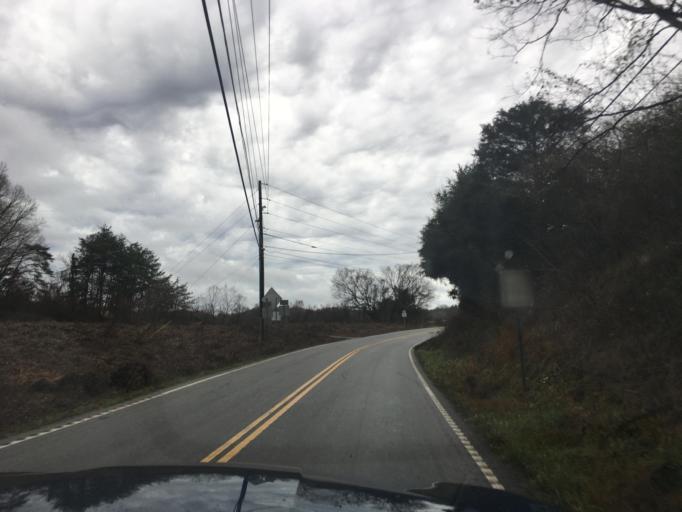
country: US
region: Tennessee
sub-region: Monroe County
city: Madisonville
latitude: 35.3728
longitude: -84.3063
